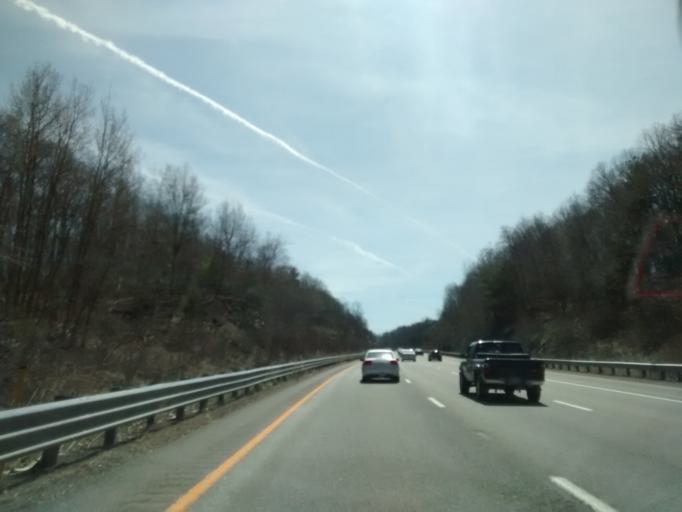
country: US
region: Massachusetts
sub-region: Worcester County
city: Southborough
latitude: 42.3005
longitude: -71.5659
